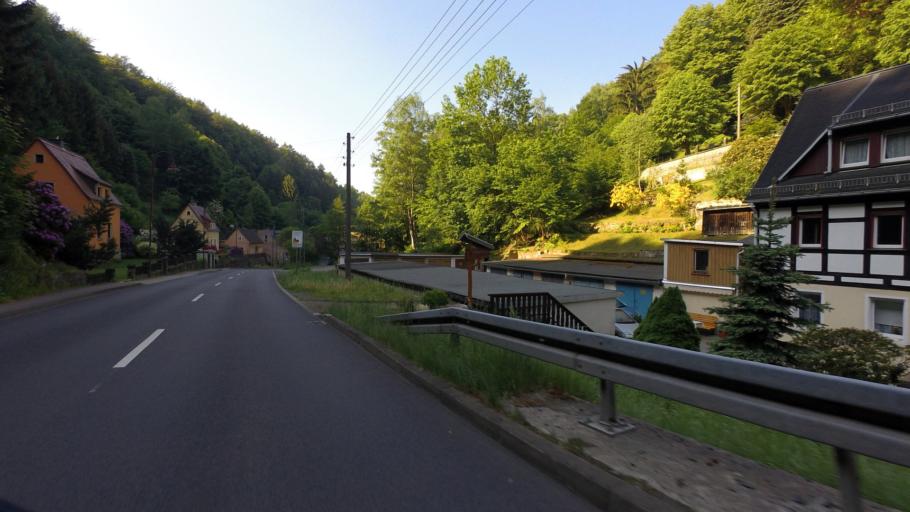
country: DE
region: Saxony
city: Bad Schandau
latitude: 50.9226
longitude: 14.1538
